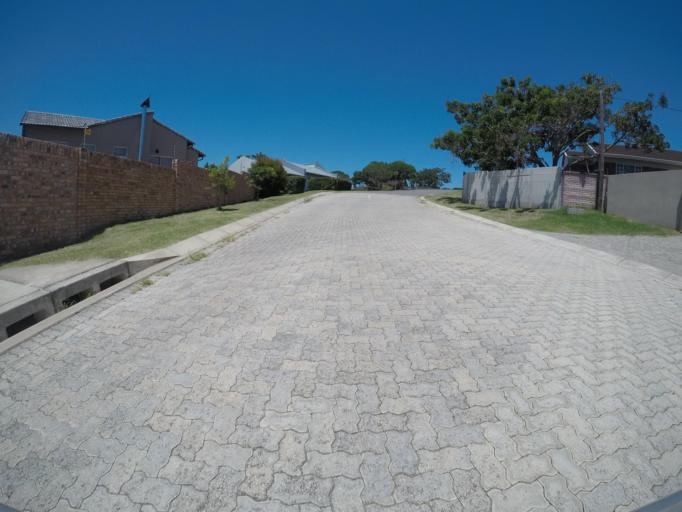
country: ZA
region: Eastern Cape
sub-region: Buffalo City Metropolitan Municipality
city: East London
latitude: -32.9550
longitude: 27.9402
